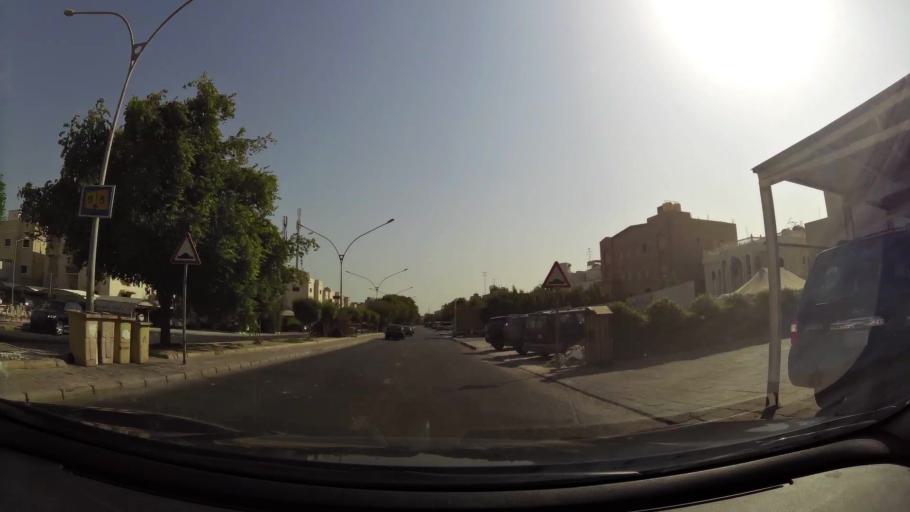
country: KW
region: Muhafazat Hawalli
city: Salwa
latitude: 29.2963
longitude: 48.0827
